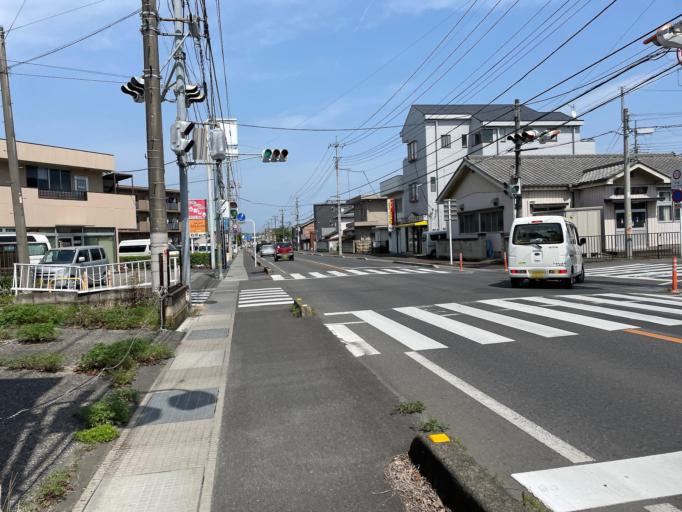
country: JP
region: Gunma
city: Ota
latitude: 36.2931
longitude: 139.3502
